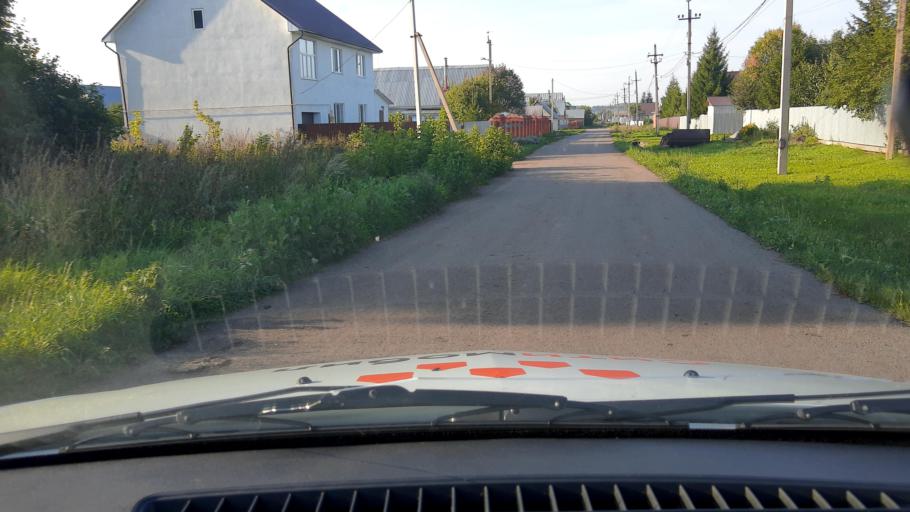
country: RU
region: Bashkortostan
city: Avdon
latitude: 54.4912
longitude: 55.8788
